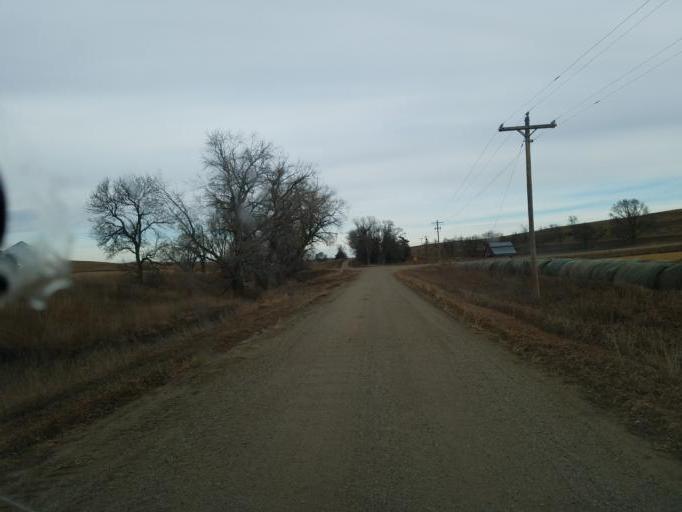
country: US
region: Nebraska
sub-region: Knox County
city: Bloomfield
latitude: 42.5567
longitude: -97.7205
